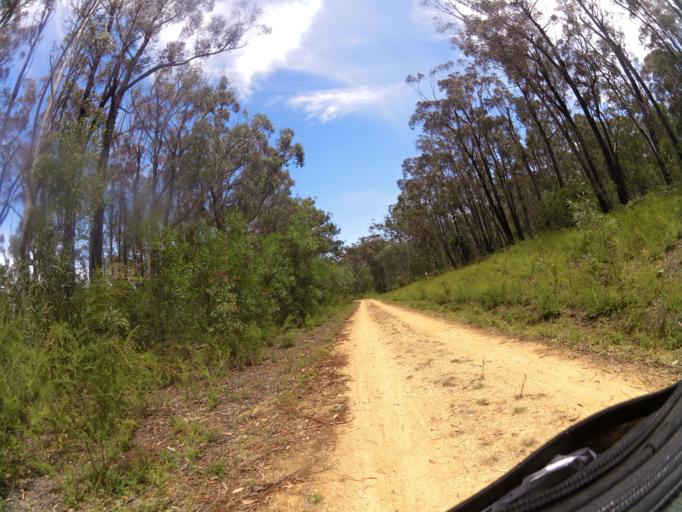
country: AU
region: Victoria
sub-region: East Gippsland
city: Lakes Entrance
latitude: -37.7437
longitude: 148.0001
